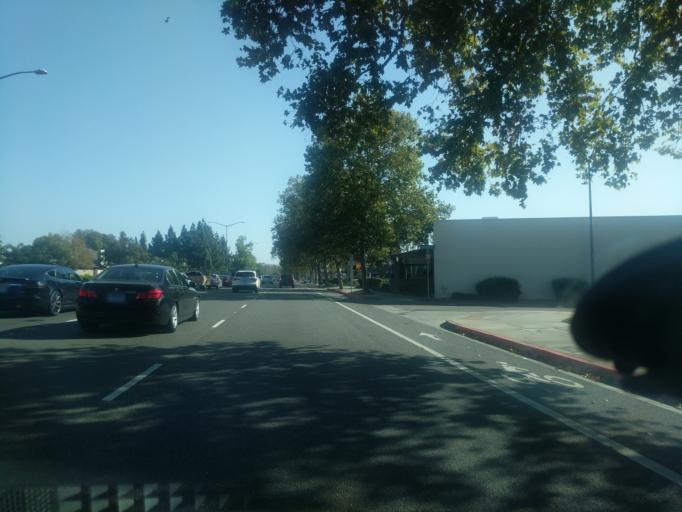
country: US
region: California
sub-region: Alameda County
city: Pleasanton
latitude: 37.6797
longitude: -121.8751
